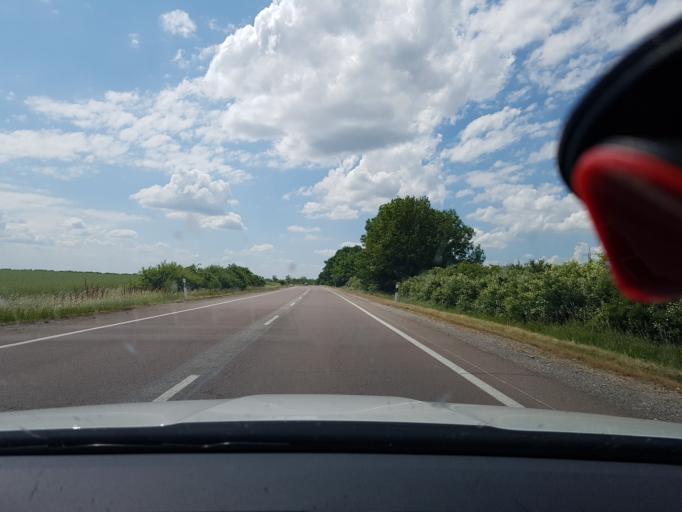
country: HU
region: Heves
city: Kompolt
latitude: 47.7626
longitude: 20.2071
